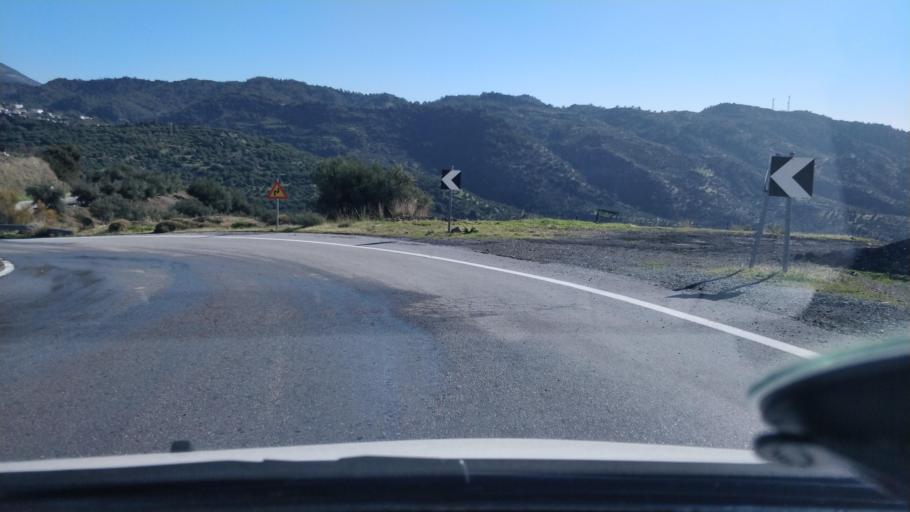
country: GR
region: Crete
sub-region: Nomos Irakleiou
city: Kastelli
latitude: 35.0333
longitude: 25.4460
